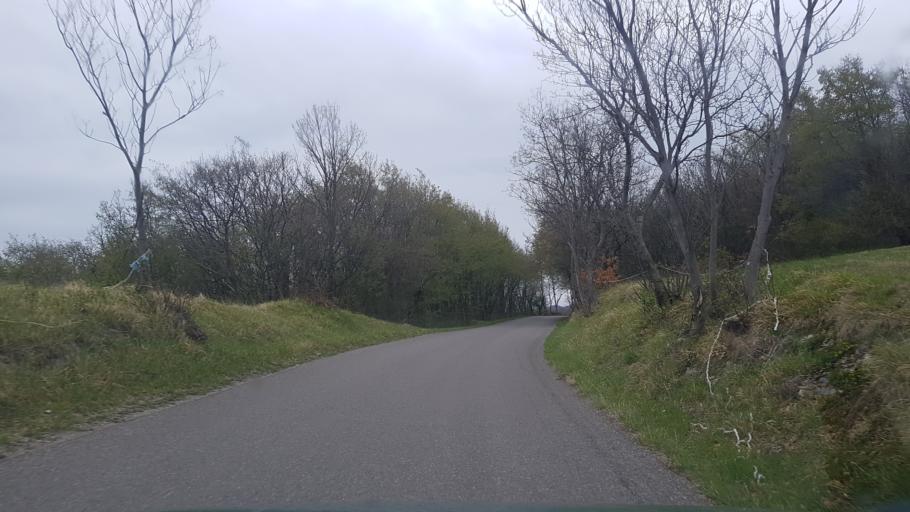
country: SI
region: Kanal
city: Deskle
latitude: 46.0426
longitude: 13.5636
